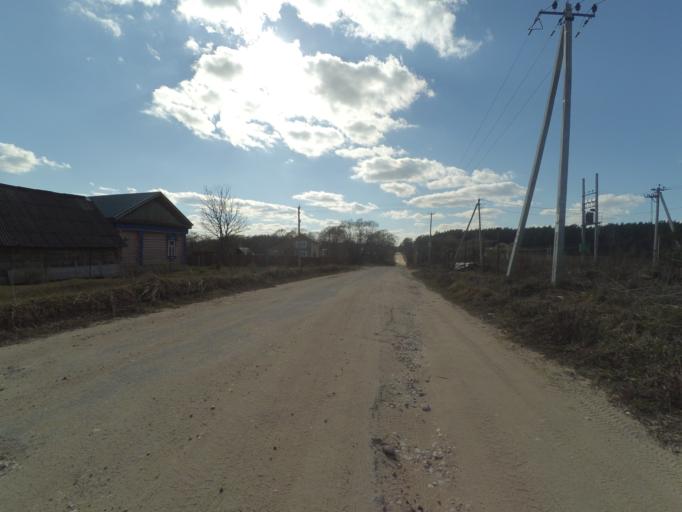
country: RU
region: Moskovskaya
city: Stupino
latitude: 54.8569
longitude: 37.9502
